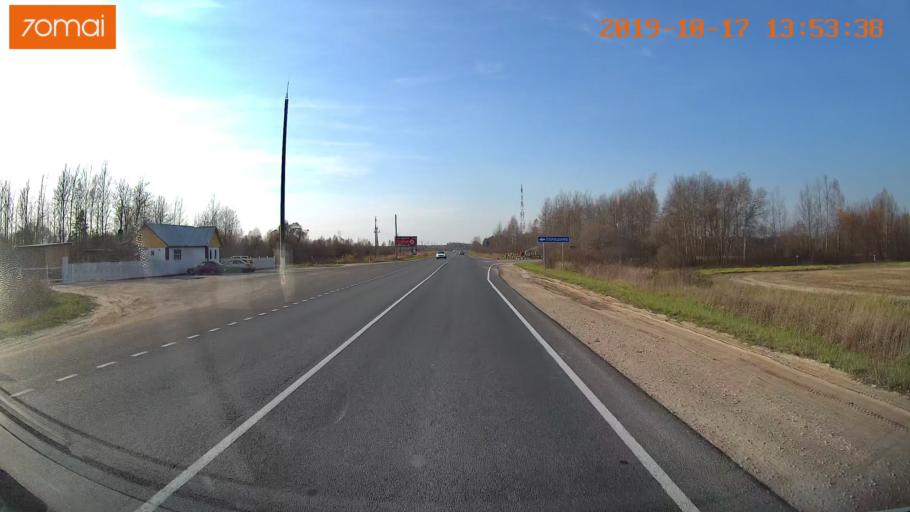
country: RU
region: Rjazan
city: Spas-Klepiki
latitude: 55.1430
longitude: 40.3358
